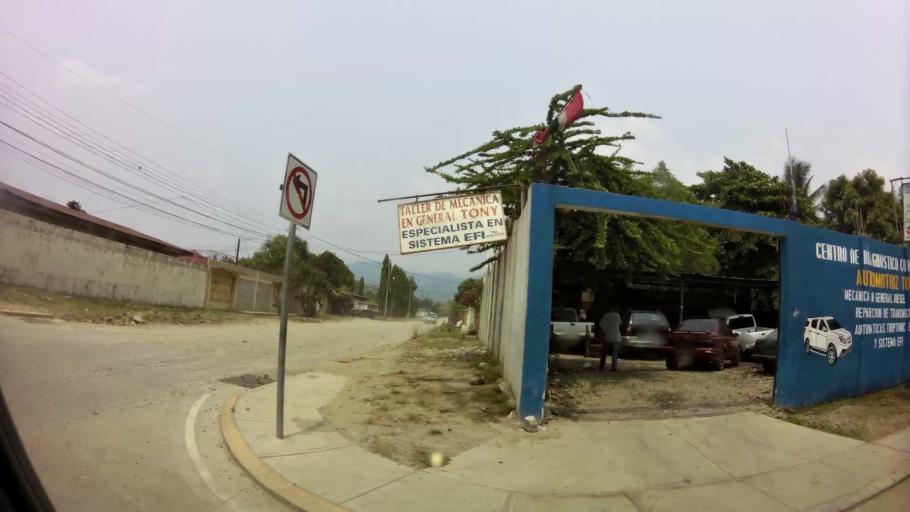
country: HN
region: Yoro
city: El Progreso
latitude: 15.4003
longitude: -87.8040
